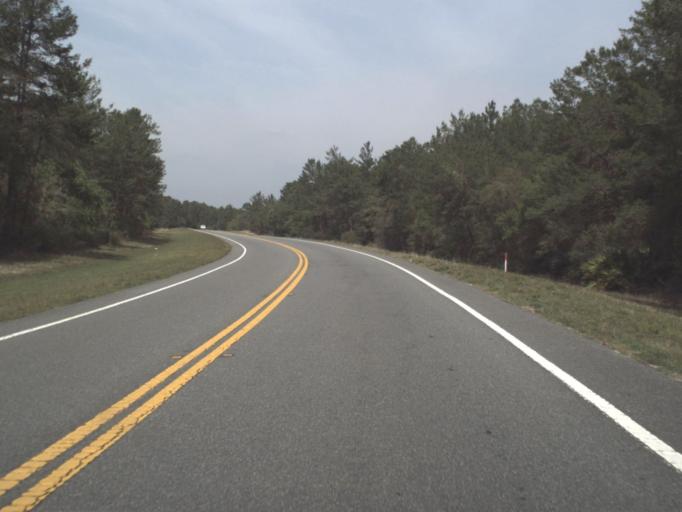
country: US
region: Florida
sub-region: Lake County
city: Astor
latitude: 29.1664
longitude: -81.6106
